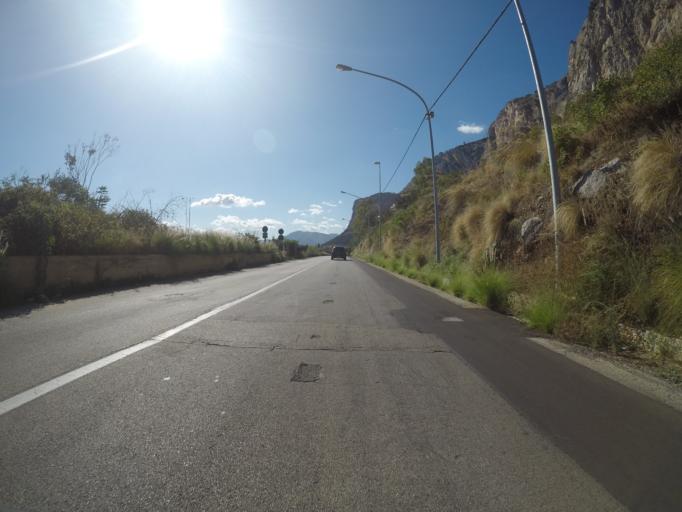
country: IT
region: Sicily
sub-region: Palermo
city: Palermo
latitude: 38.1754
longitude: 13.3661
